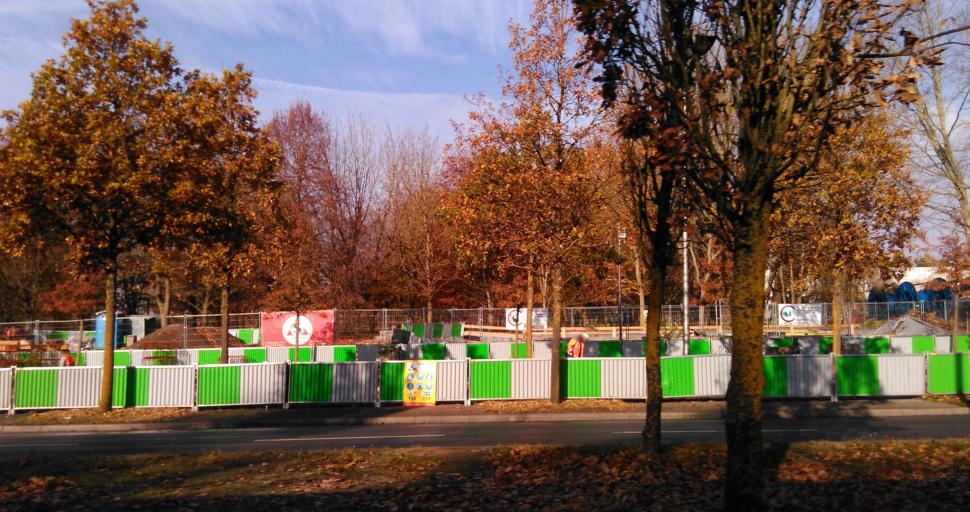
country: LU
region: Luxembourg
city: Kirchberg
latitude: 49.6242
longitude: 6.1580
